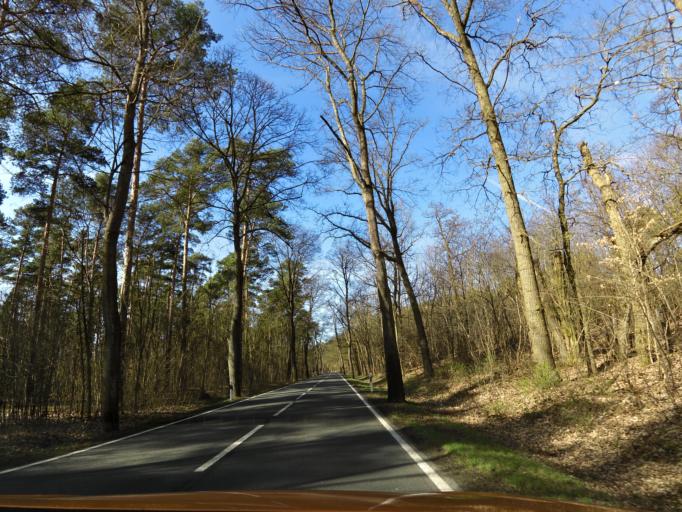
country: DE
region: Brandenburg
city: Beelitz
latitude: 52.2348
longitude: 12.9396
